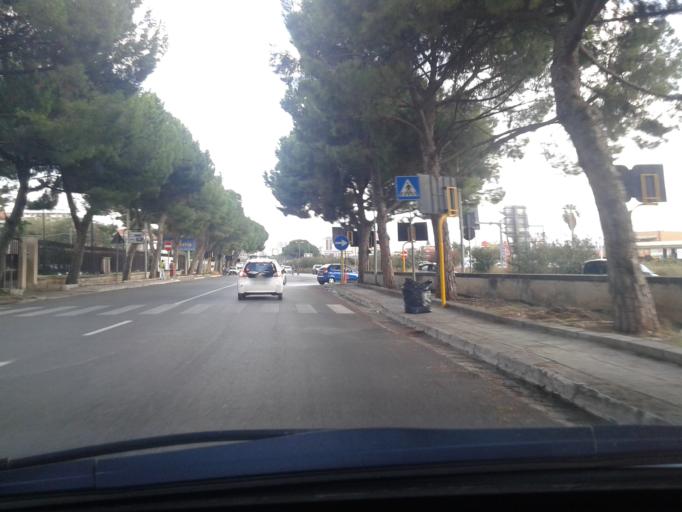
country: IT
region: Sicily
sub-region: Palermo
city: Palermo
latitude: 38.1520
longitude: 13.3230
